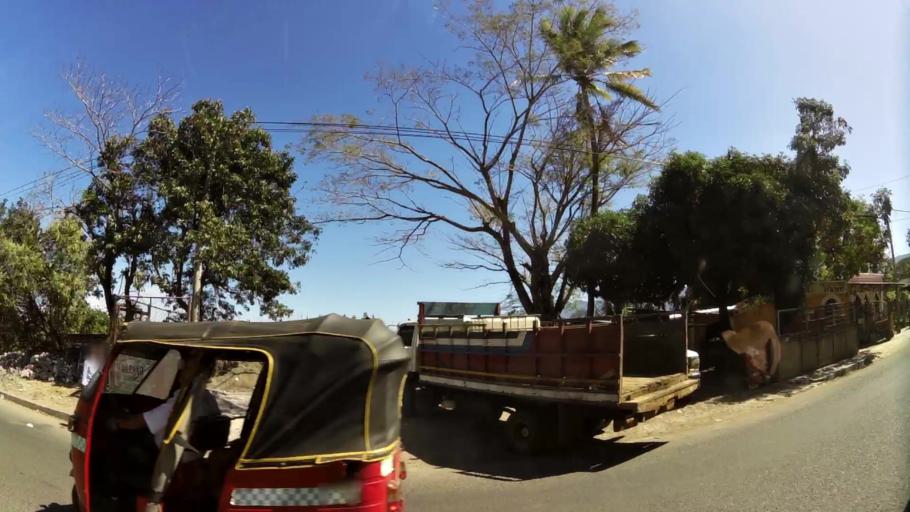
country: SV
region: Ahuachapan
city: Ahuachapan
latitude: 13.9347
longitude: -89.8557
